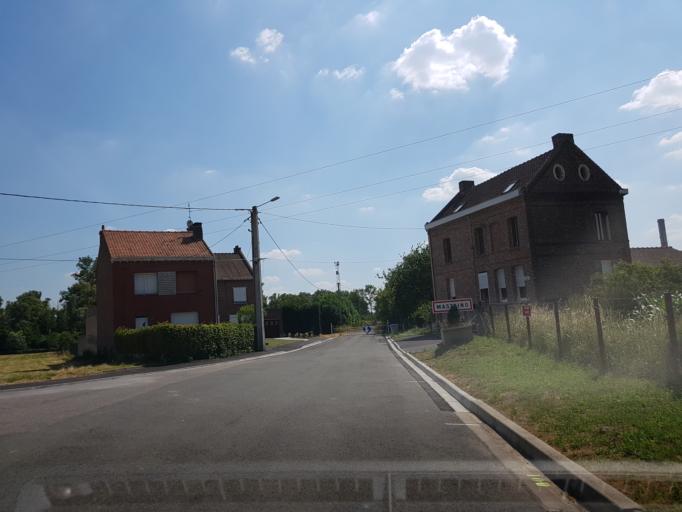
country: FR
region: Nord-Pas-de-Calais
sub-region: Departement du Nord
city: Roeulx
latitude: 50.3026
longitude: 3.3263
